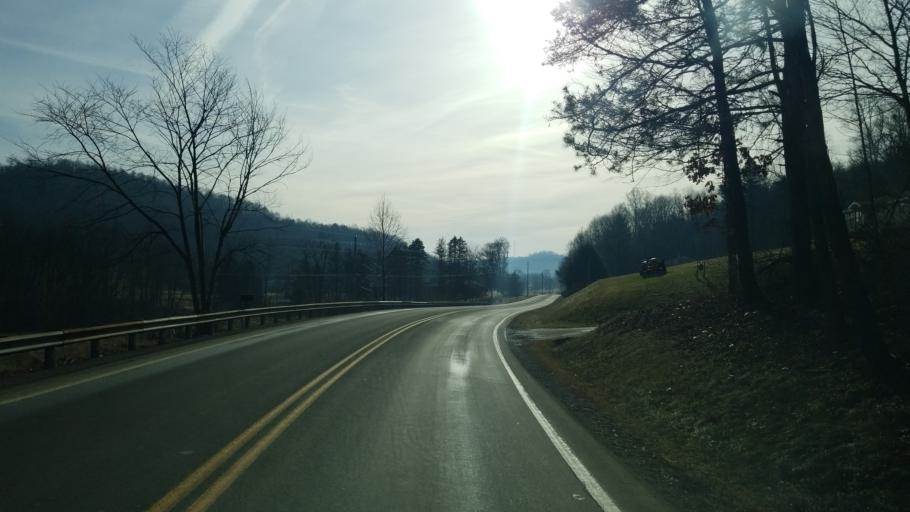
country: US
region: Pennsylvania
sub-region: Indiana County
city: Chevy Chase Heights
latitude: 40.7731
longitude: -79.1531
